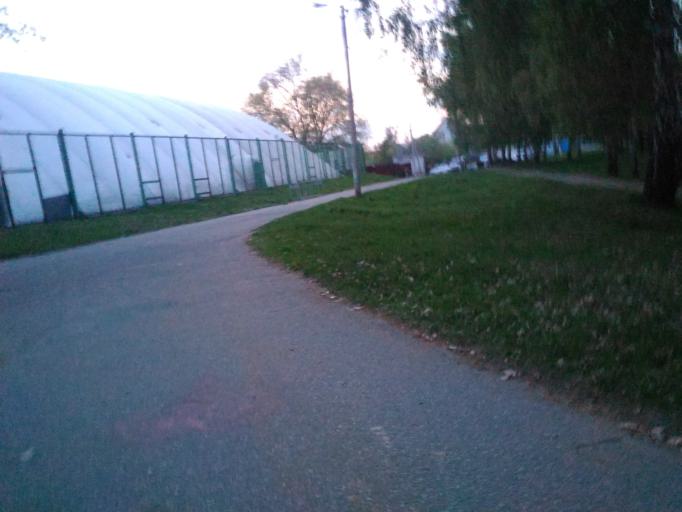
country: RU
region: Ulyanovsk
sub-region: Ulyanovskiy Rayon
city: Ulyanovsk
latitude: 54.2760
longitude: 48.3526
